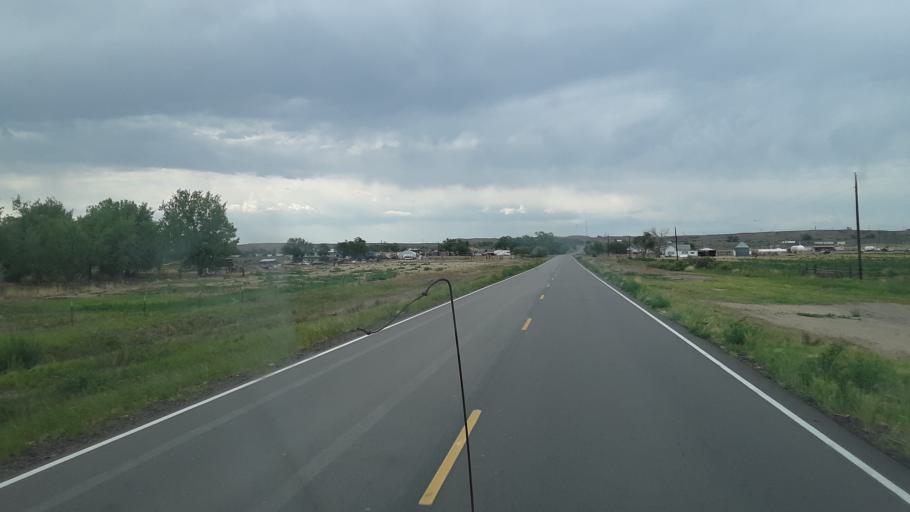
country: US
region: Colorado
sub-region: Otero County
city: Fowler
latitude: 38.1442
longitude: -104.0229
